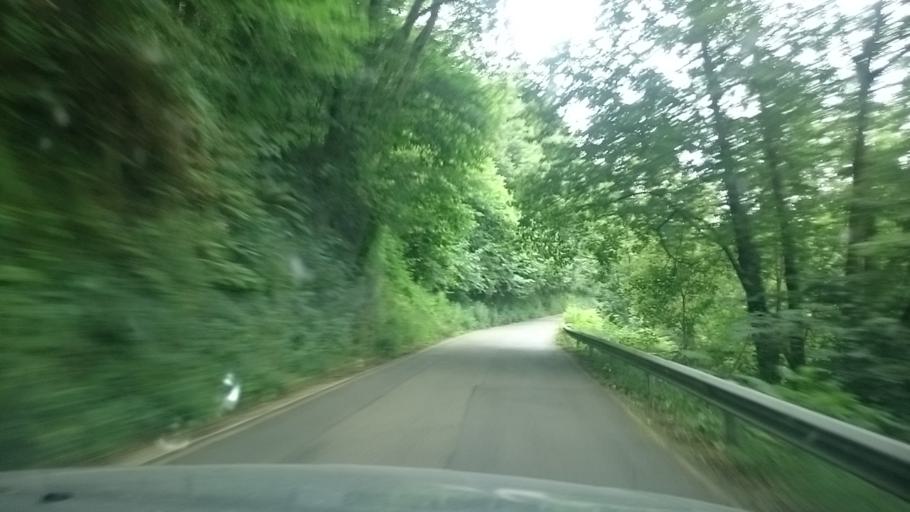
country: ES
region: Asturias
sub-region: Province of Asturias
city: Oviedo
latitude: 43.3048
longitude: -5.8247
